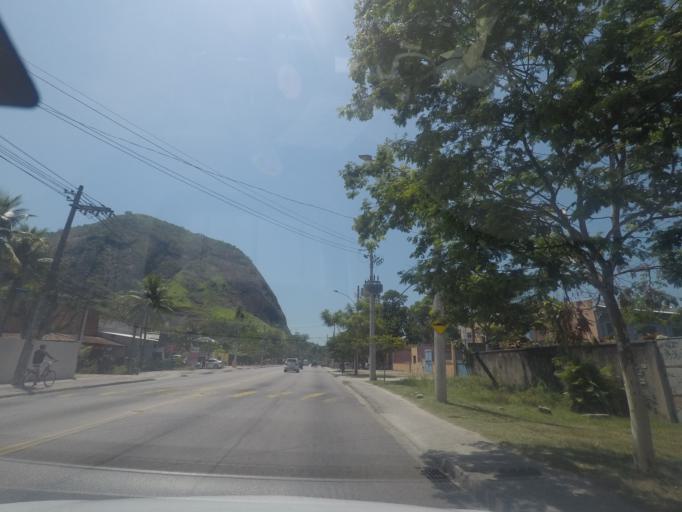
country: BR
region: Rio de Janeiro
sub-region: Nilopolis
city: Nilopolis
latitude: -22.9871
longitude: -43.4565
